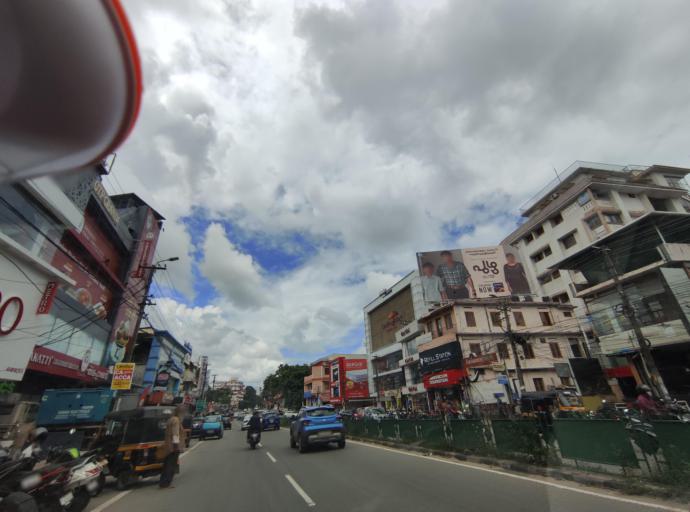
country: IN
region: Kerala
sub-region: Thiruvananthapuram
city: Thiruvananthapuram
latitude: 8.5244
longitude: 76.9398
